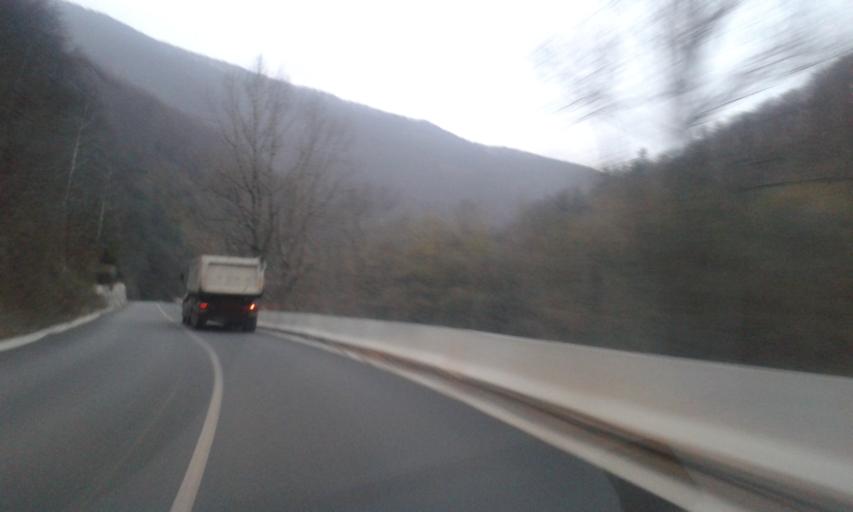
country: RO
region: Gorj
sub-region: Comuna Bumbesti-Jiu
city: Bumbesti-Jiu
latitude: 45.2358
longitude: 23.3892
